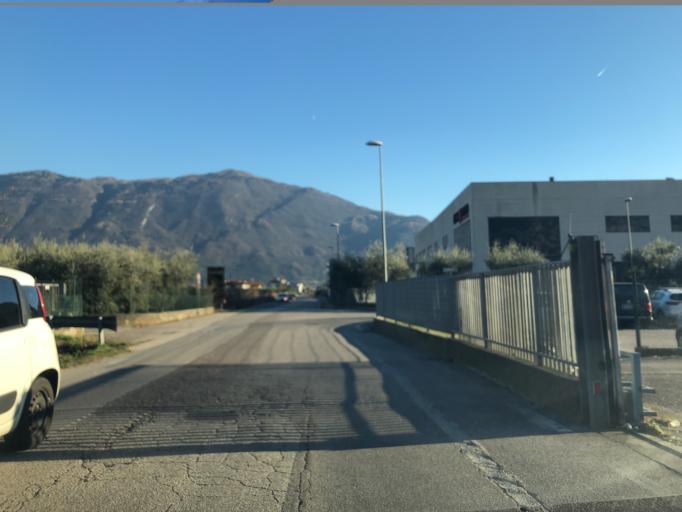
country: IT
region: Trentino-Alto Adige
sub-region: Provincia di Trento
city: Arco
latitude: 45.9136
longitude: 10.8629
